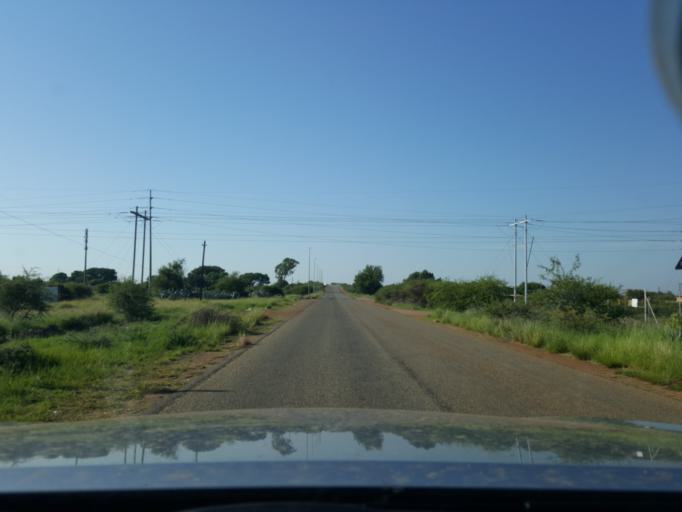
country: ZA
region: North-West
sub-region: Ngaka Modiri Molema District Municipality
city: Mahikeng
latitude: -25.8458
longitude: 25.6772
